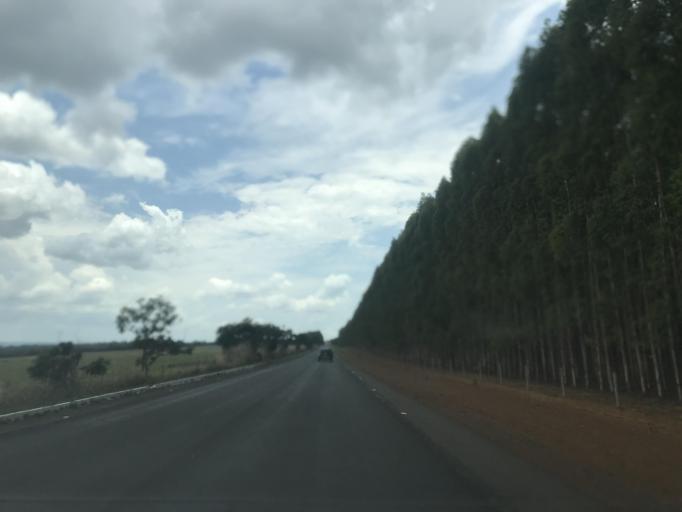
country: BR
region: Goias
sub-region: Vianopolis
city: Vianopolis
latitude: -16.9277
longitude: -48.5580
